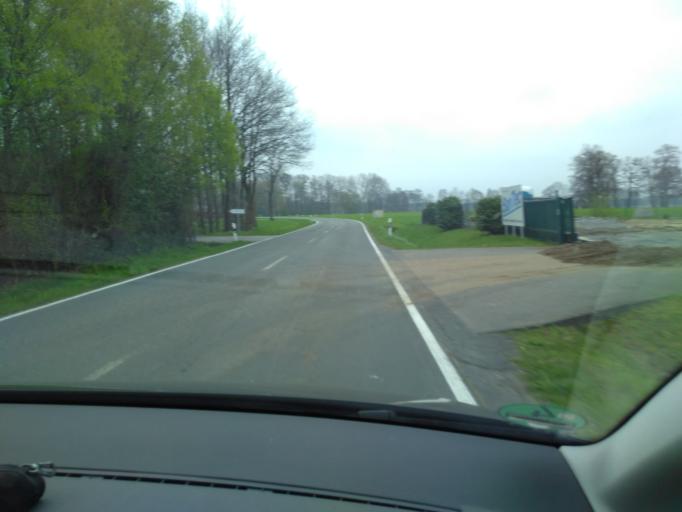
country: DE
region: North Rhine-Westphalia
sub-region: Regierungsbezirk Detmold
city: Verl
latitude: 51.8539
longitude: 8.5057
